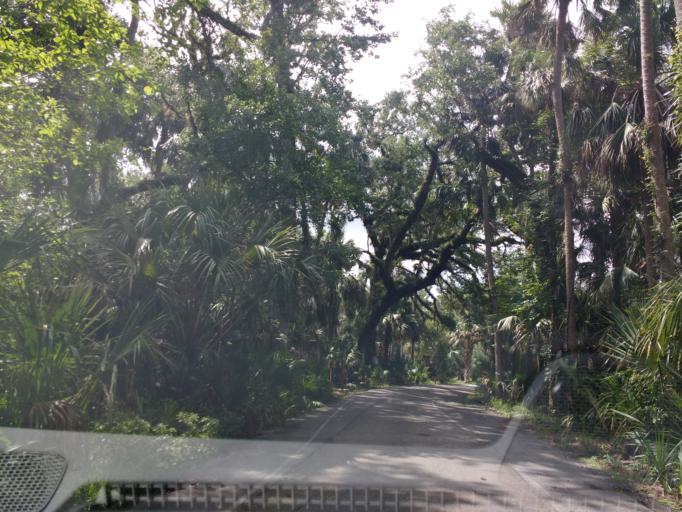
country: US
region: Florida
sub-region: Highlands County
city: Sebring
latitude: 27.4723
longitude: -81.5523
